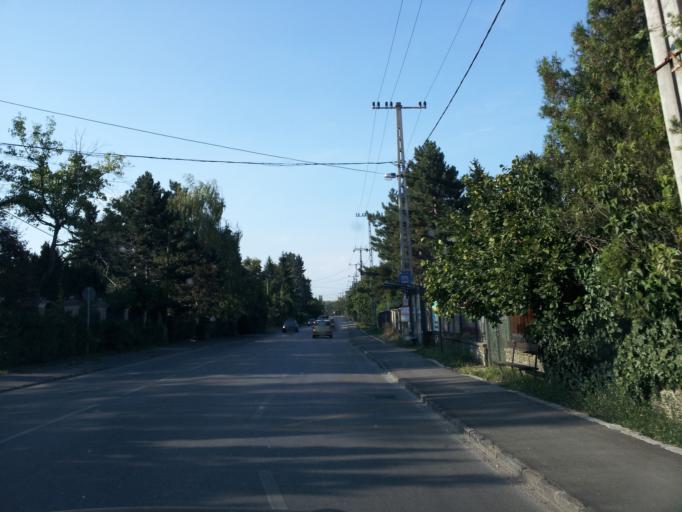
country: HU
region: Pest
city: Leanyfalu
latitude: 47.6950
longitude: 19.0883
